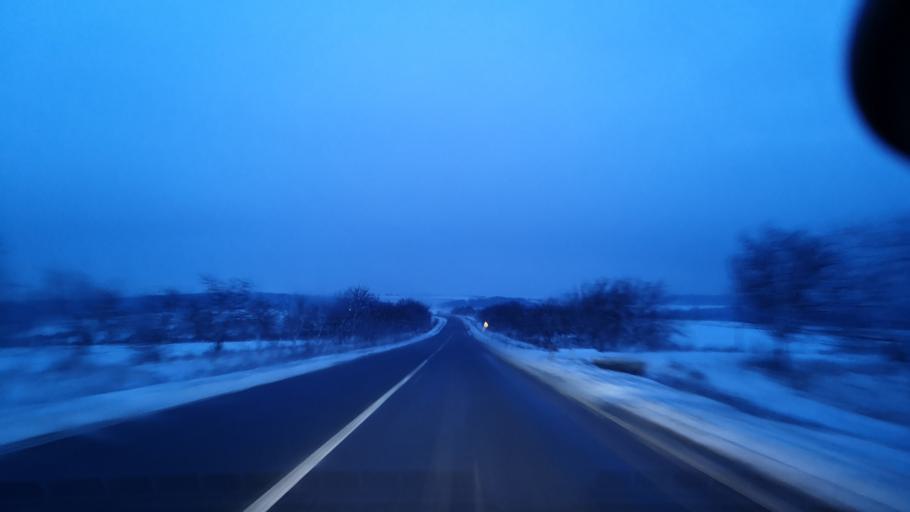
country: MD
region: Rezina
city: Saharna
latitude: 47.6132
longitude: 28.8313
